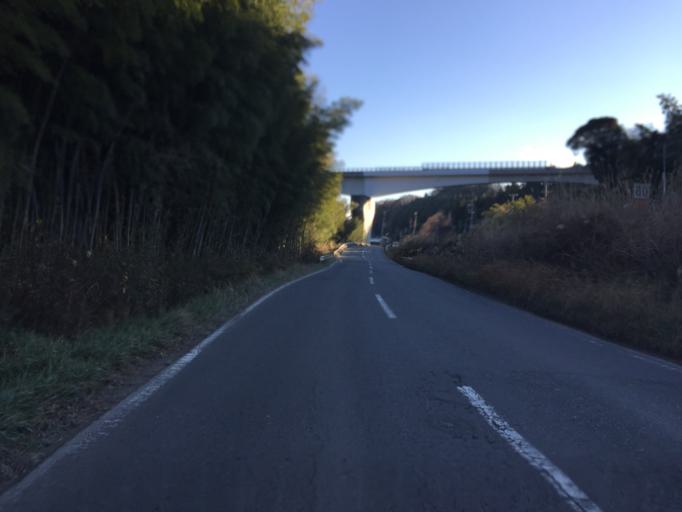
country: JP
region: Fukushima
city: Iwaki
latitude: 37.0980
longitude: 140.8596
